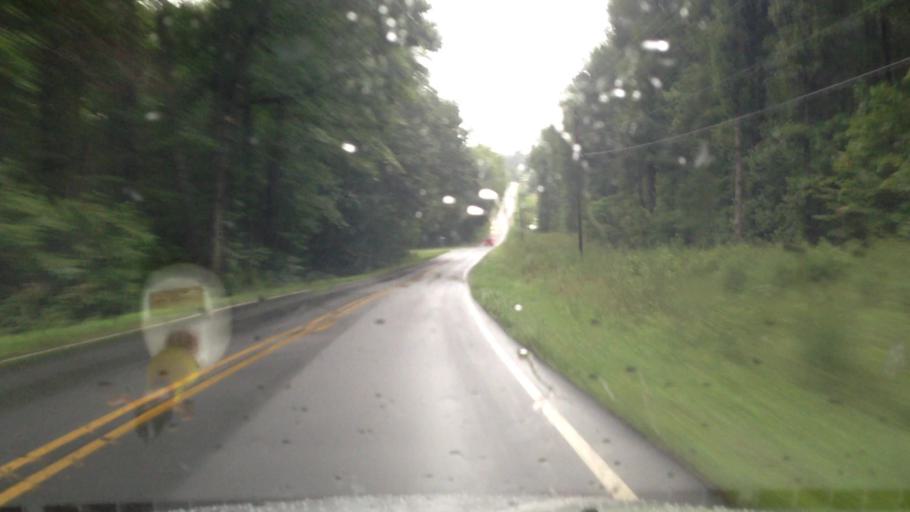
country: US
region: North Carolina
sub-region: Rockingham County
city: Reidsville
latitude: 36.2647
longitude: -79.7295
